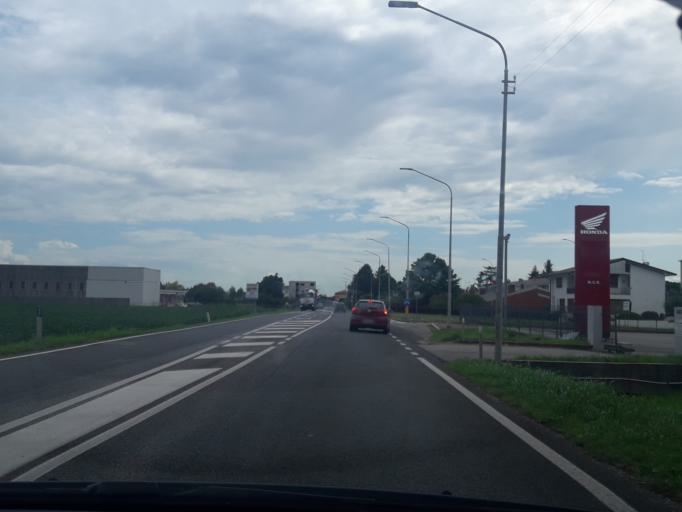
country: IT
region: Friuli Venezia Giulia
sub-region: Provincia di Udine
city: Udine
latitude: 46.0258
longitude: 13.2597
